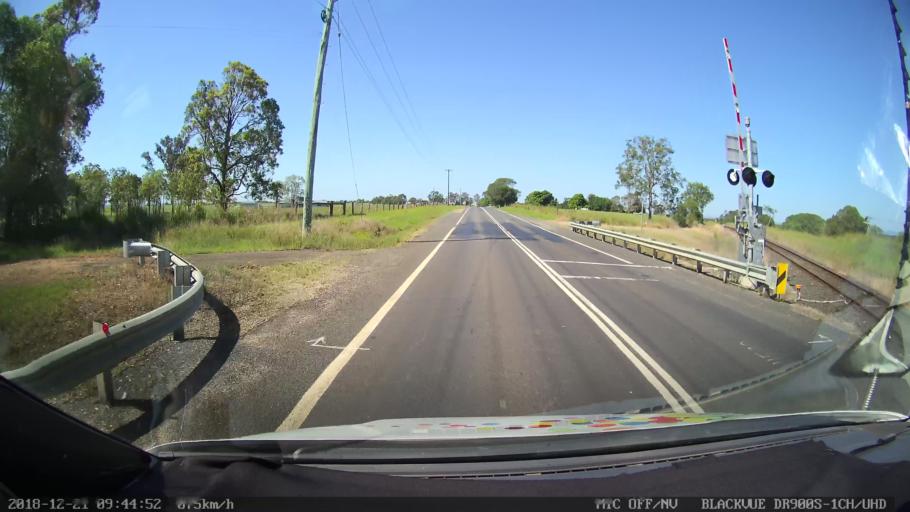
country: AU
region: New South Wales
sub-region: Clarence Valley
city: Grafton
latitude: -29.6223
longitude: 152.9307
